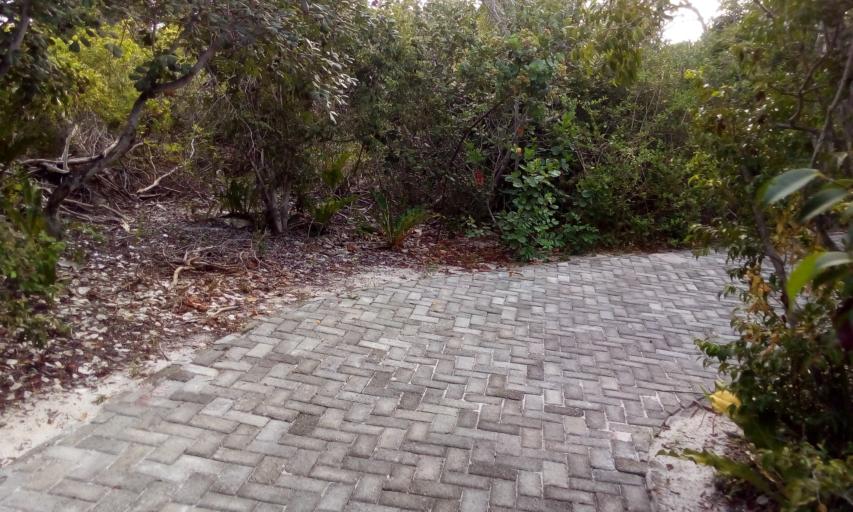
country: BR
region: Bahia
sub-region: Mata De Sao Joao
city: Mata de Sao Joao
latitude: -12.5667
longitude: -38.0022
